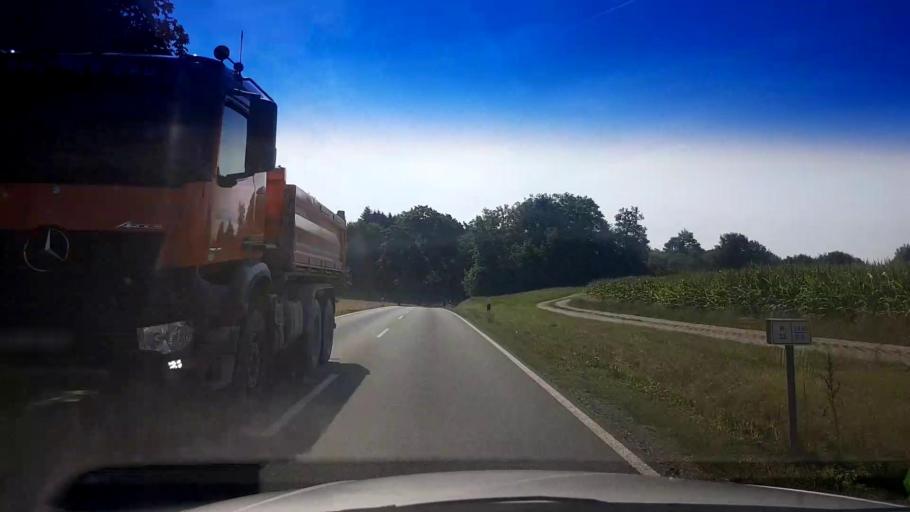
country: DE
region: Bavaria
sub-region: Upper Franconia
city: Hollfeld
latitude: 49.9454
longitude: 11.3325
